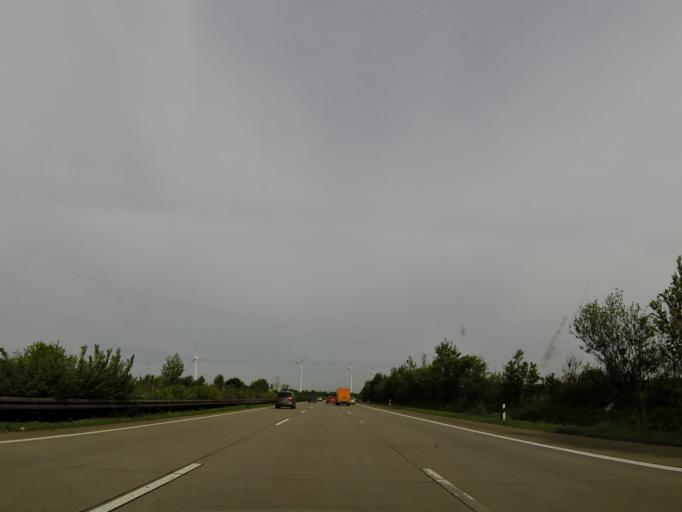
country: DE
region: Lower Saxony
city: Harsum
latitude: 52.1935
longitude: 9.9516
